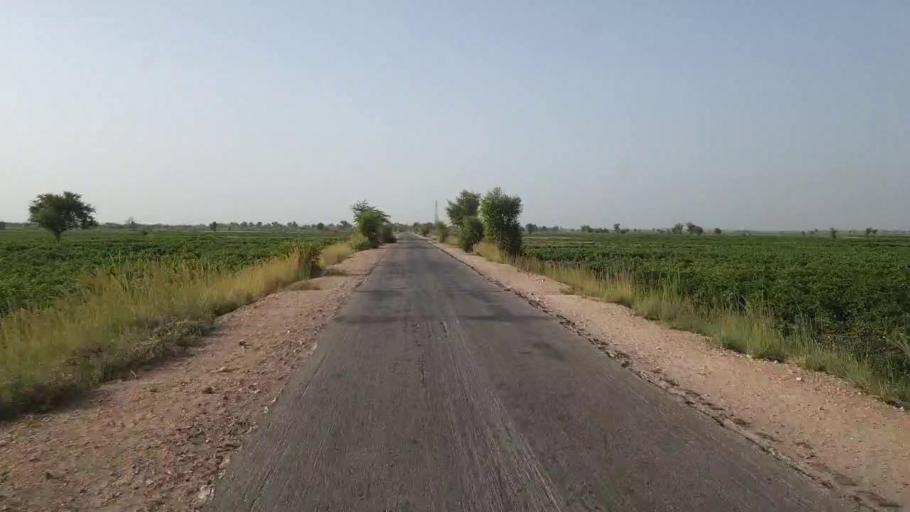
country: PK
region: Sindh
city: Jam Sahib
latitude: 26.4731
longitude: 68.8596
